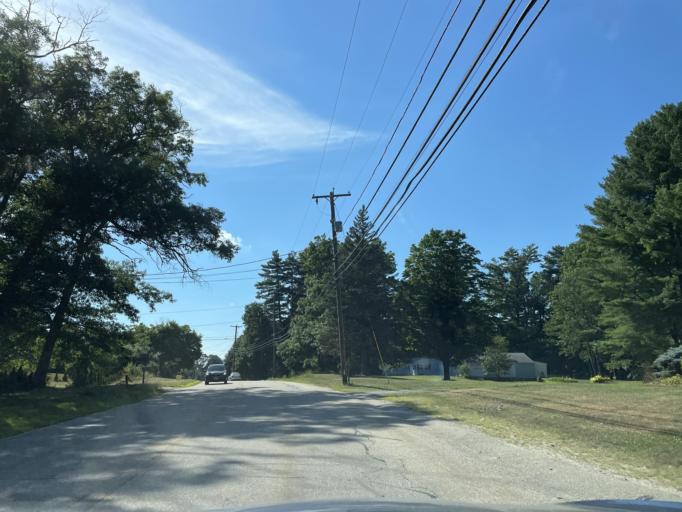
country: US
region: Massachusetts
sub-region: Worcester County
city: Oxford
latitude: 42.1153
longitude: -71.8835
